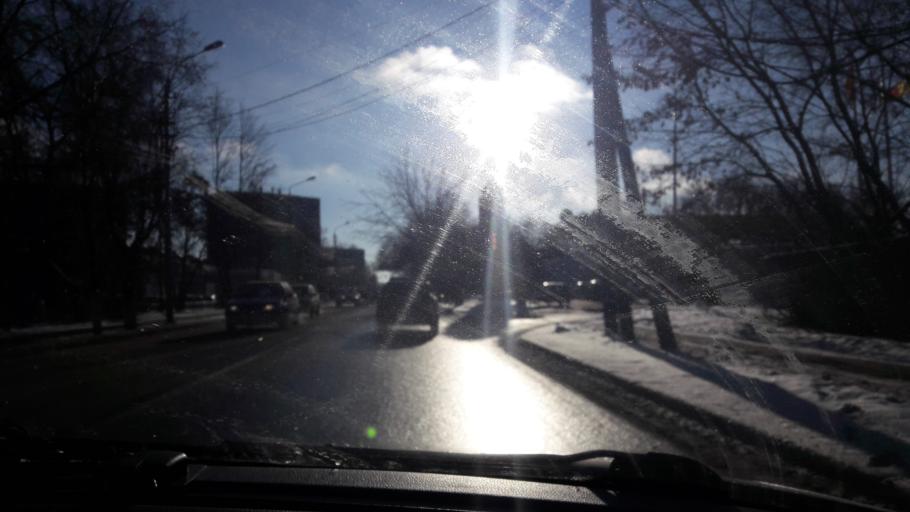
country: RU
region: Tula
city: Tula
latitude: 54.1753
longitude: 37.6240
